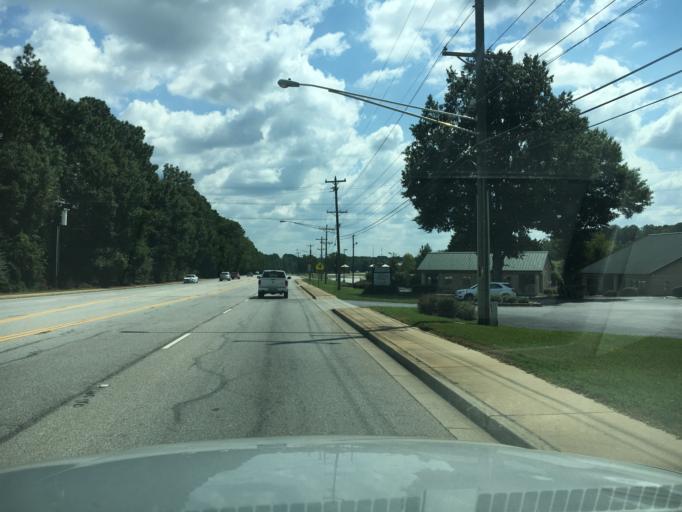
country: US
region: South Carolina
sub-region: Greenwood County
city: Greenwood
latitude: 34.1942
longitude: -82.1886
